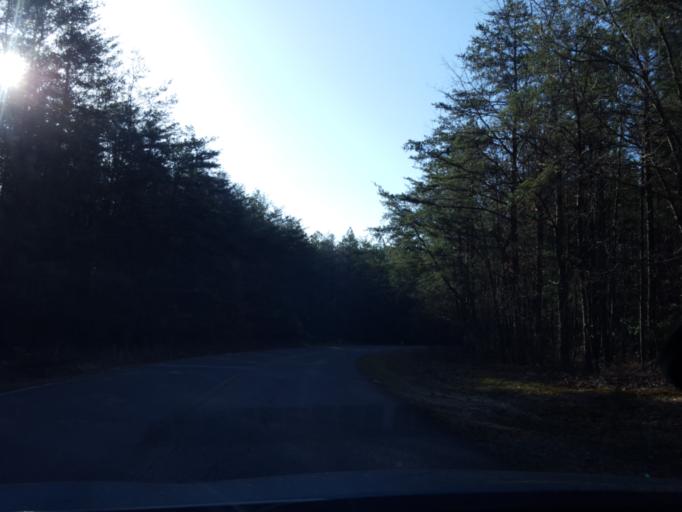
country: US
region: Maryland
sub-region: Prince George's County
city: Brandywine
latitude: 38.6521
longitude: -76.8318
